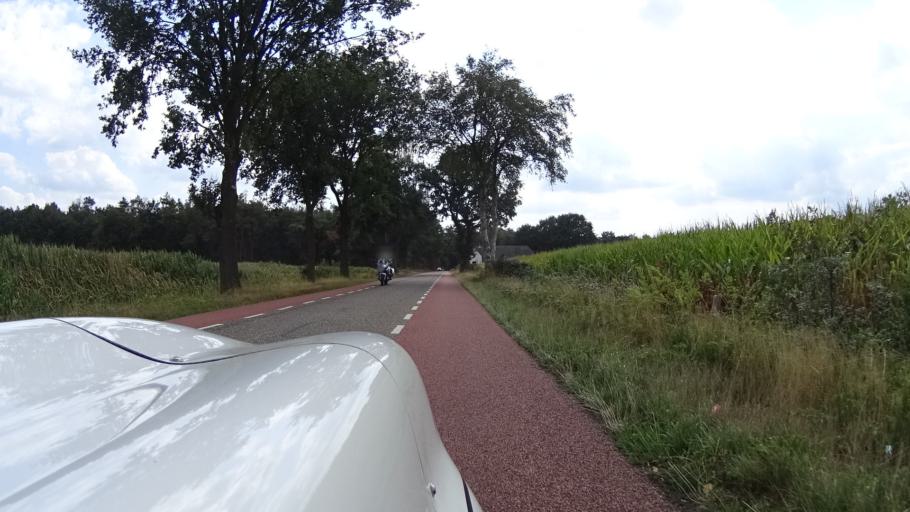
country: NL
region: North Brabant
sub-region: Gemeente Bernheze
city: Loosbroek
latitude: 51.6744
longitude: 5.4633
